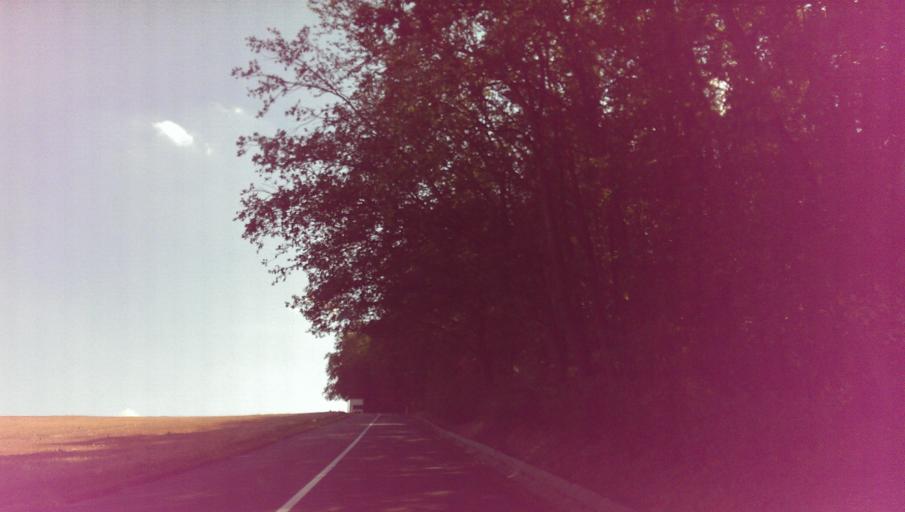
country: CZ
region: Zlin
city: Tlumacov
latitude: 49.2640
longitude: 17.5449
